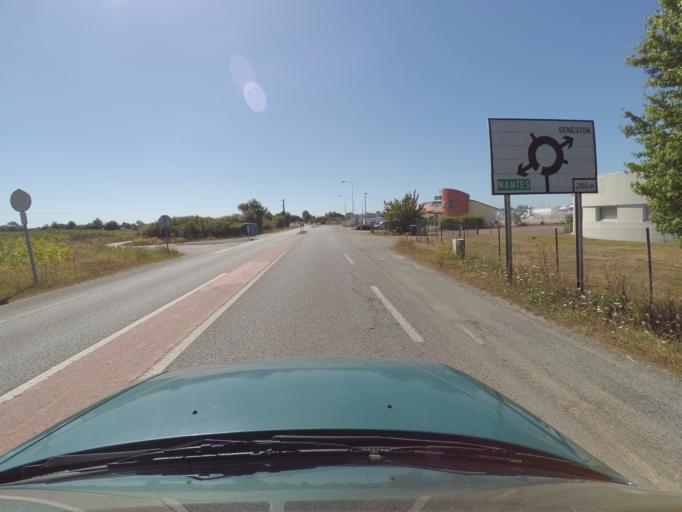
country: FR
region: Pays de la Loire
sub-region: Departement de la Loire-Atlantique
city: Les Sorinieres
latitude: 47.1141
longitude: -1.5407
